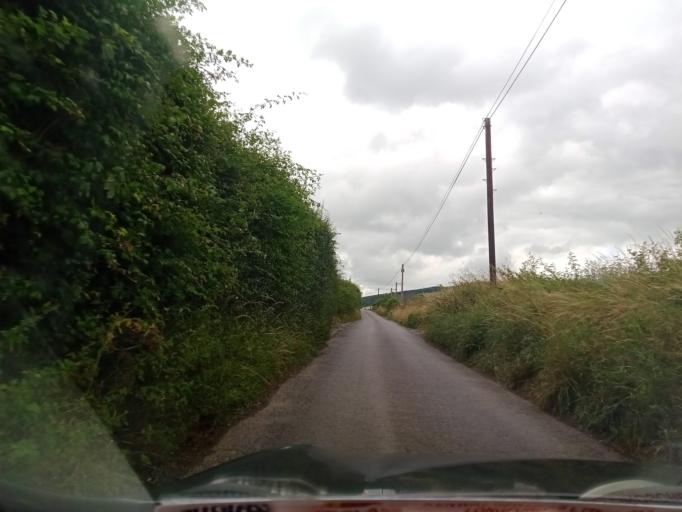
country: IE
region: Leinster
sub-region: Laois
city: Stradbally
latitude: 52.9593
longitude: -7.1951
